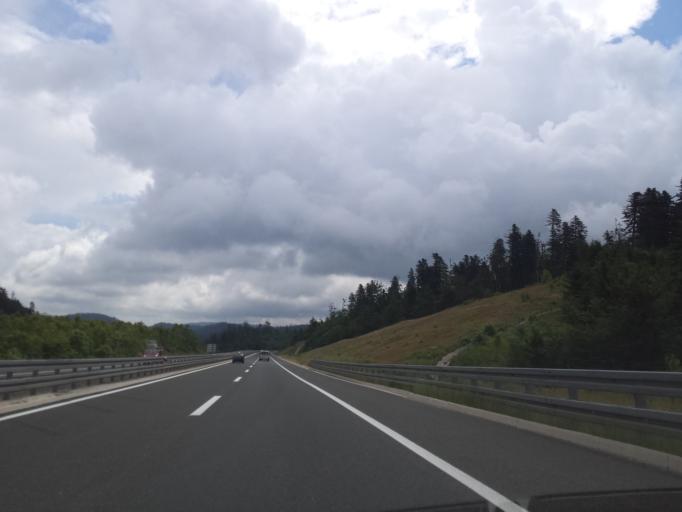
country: HR
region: Primorsko-Goranska
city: Hreljin
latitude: 45.3180
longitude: 14.6790
